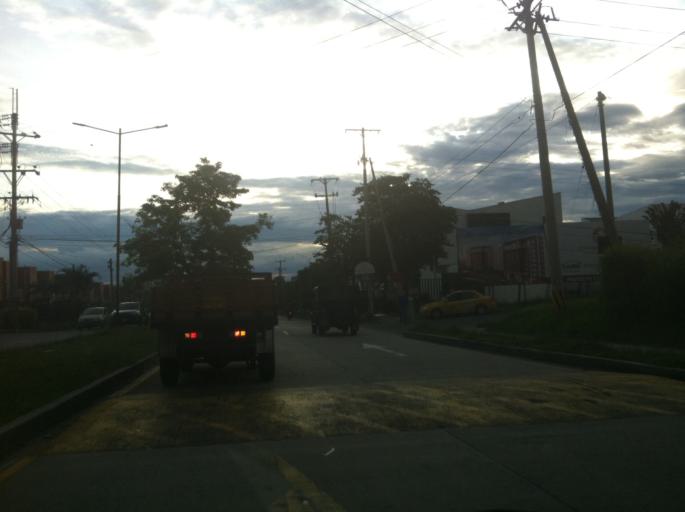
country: CO
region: Quindio
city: Calarca
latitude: 4.5657
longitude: -75.6538
